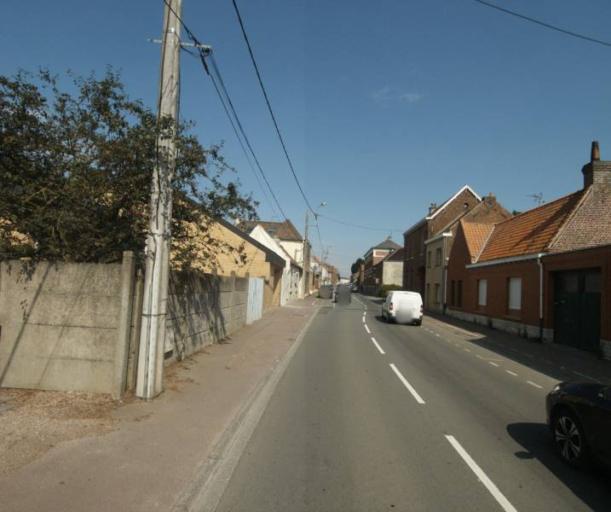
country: FR
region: Nord-Pas-de-Calais
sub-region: Departement du Nord
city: Sainghin-en-Weppes
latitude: 50.5649
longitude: 2.8960
